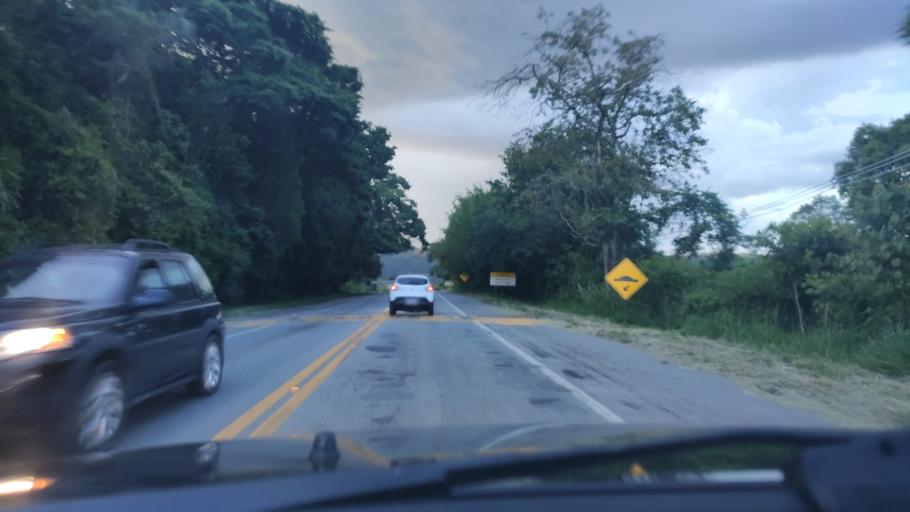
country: BR
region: Sao Paulo
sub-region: Braganca Paulista
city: Braganca Paulista
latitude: -22.8487
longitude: -46.5454
